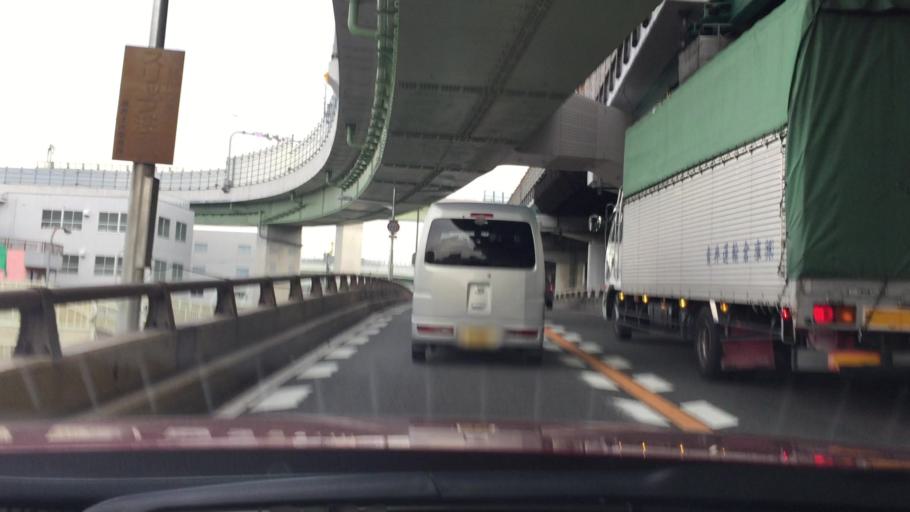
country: JP
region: Osaka
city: Kadoma
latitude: 34.7529
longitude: 135.5764
